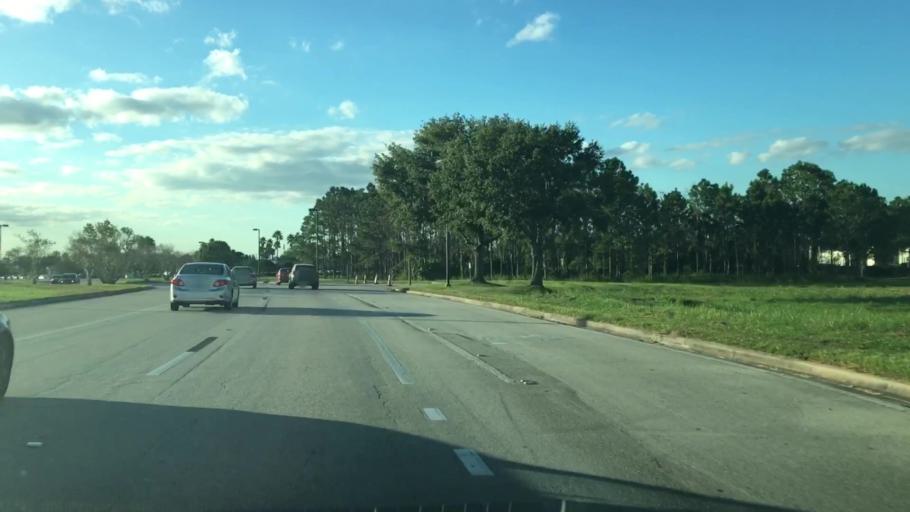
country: US
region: Florida
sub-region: Orange County
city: Conway
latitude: 28.4679
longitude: -81.3054
